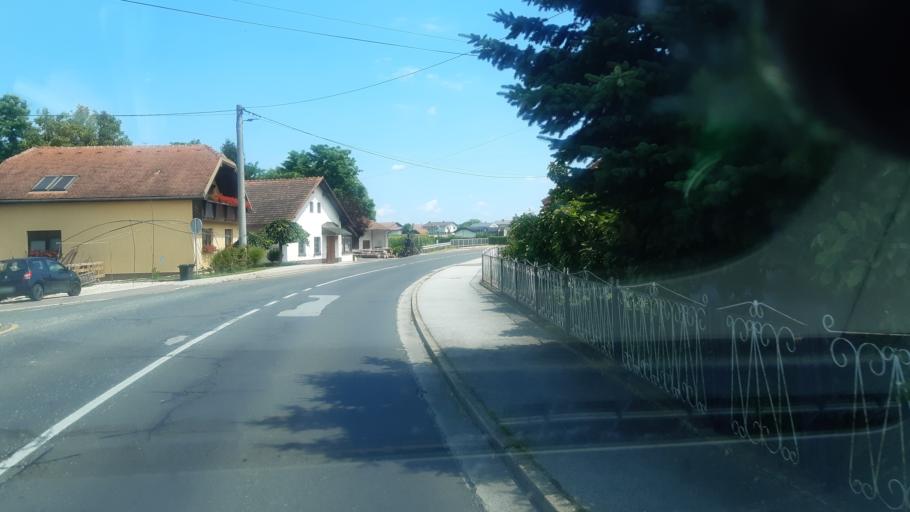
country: SI
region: Murska Sobota
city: Murska Sobota
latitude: 46.6862
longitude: 16.1848
